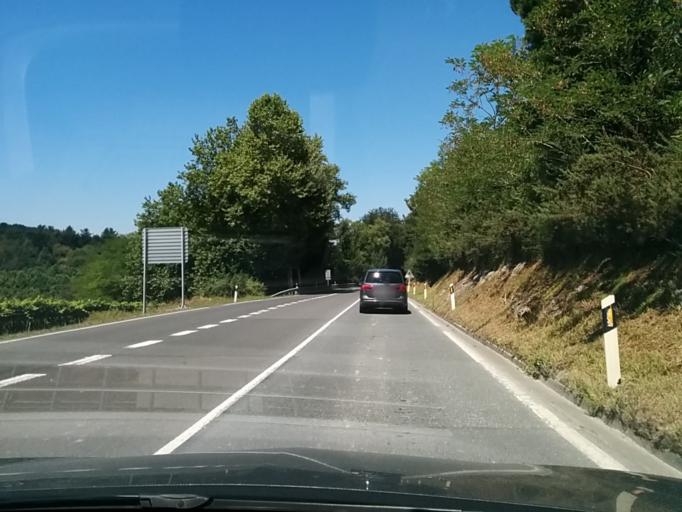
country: ES
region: Basque Country
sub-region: Provincia de Guipuzcoa
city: Orio
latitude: 43.2735
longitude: -2.1385
